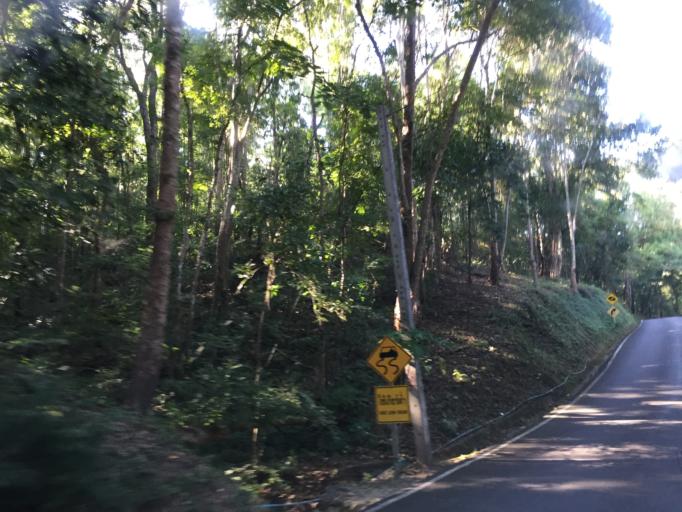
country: TH
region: Chiang Mai
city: Chiang Mai
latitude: 18.8033
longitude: 98.9425
